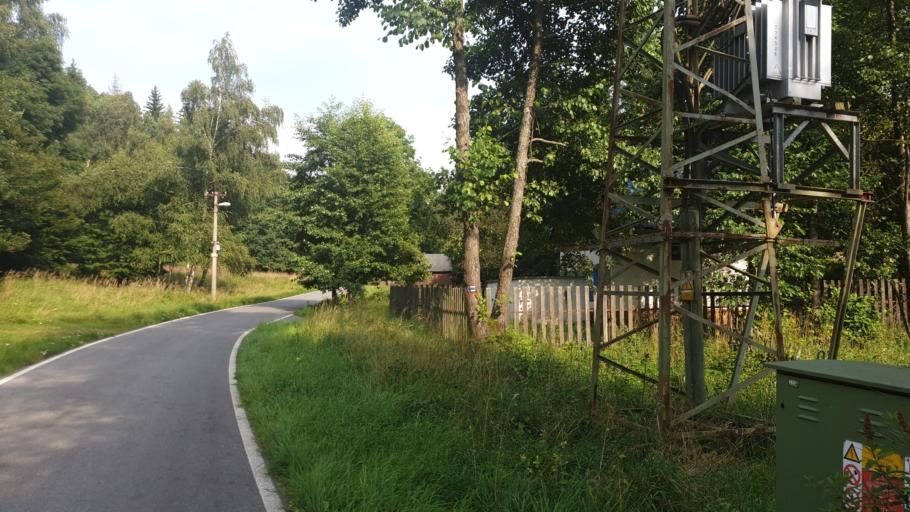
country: CZ
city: Kamenicky Senov
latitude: 50.7896
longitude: 14.5039
